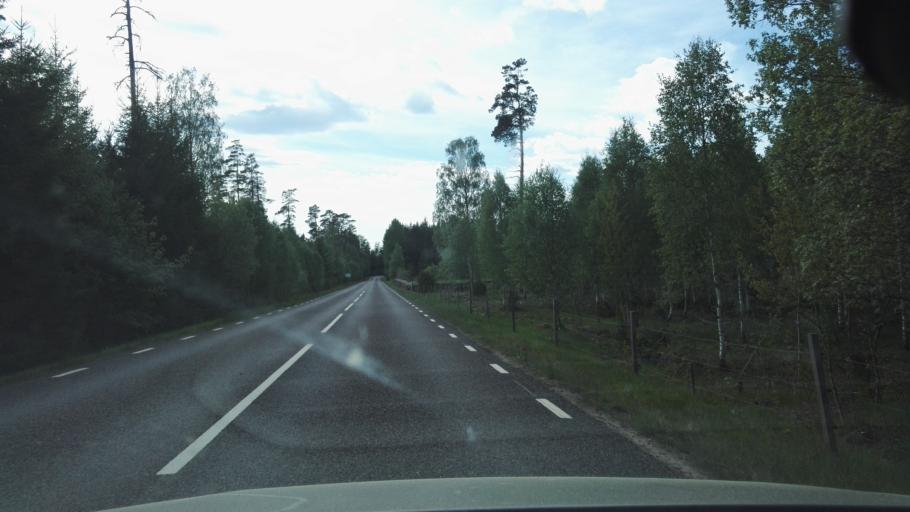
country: SE
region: Kronoberg
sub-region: Vaxjo Kommun
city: Braas
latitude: 57.0640
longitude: 15.0230
